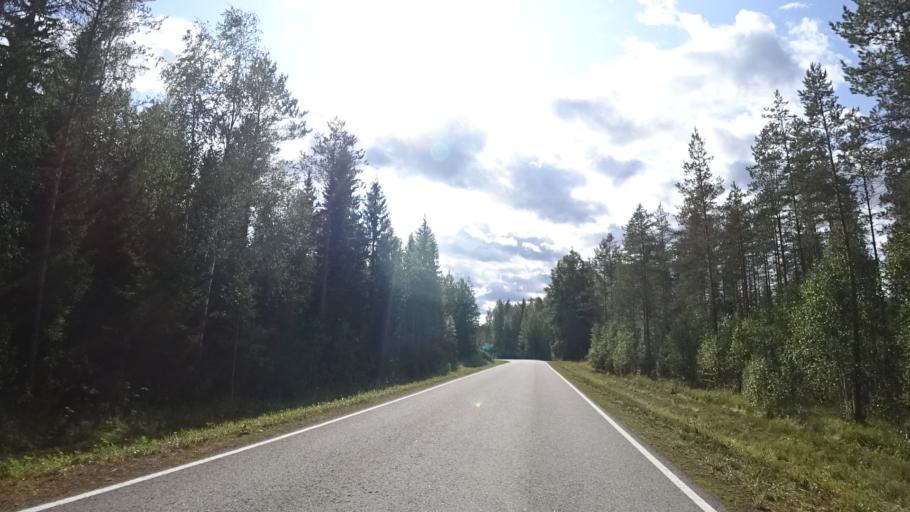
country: RU
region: Republic of Karelia
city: Vyartsilya
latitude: 62.2307
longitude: 30.6763
